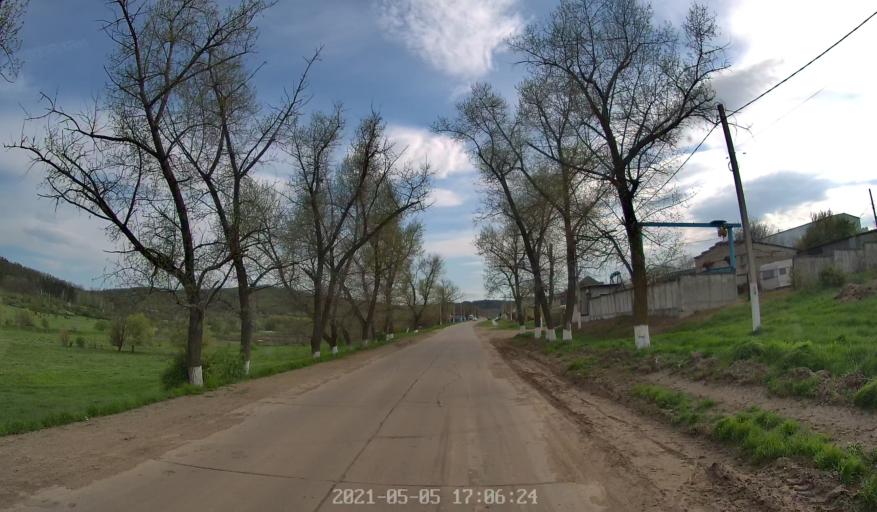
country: MD
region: Chisinau
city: Vadul lui Voda
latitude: 47.0205
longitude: 29.1396
